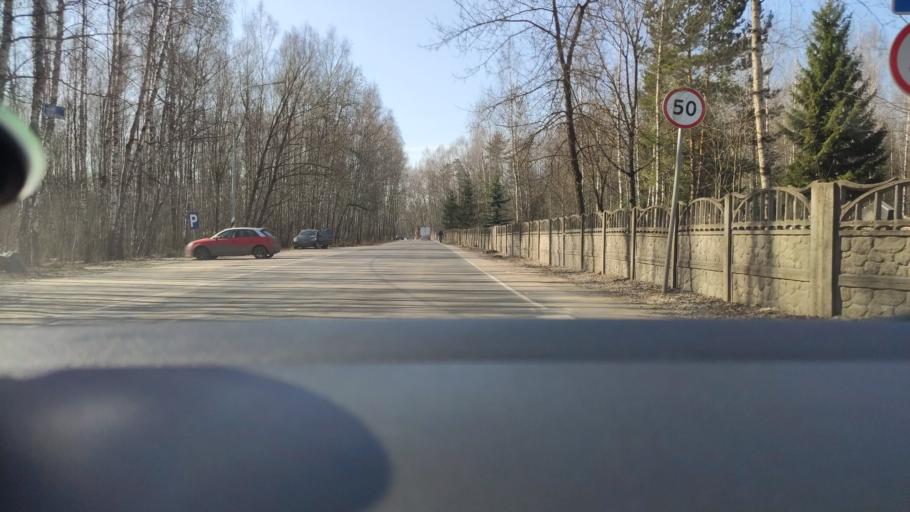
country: RU
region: Moskovskaya
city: Elektrostal'
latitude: 55.7707
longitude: 38.4090
